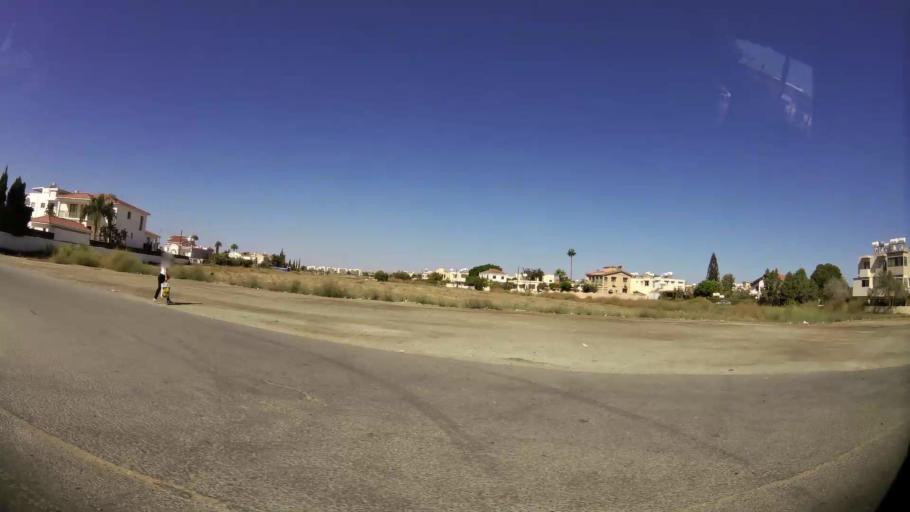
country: CY
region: Larnaka
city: Livadia
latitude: 34.9559
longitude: 33.6526
